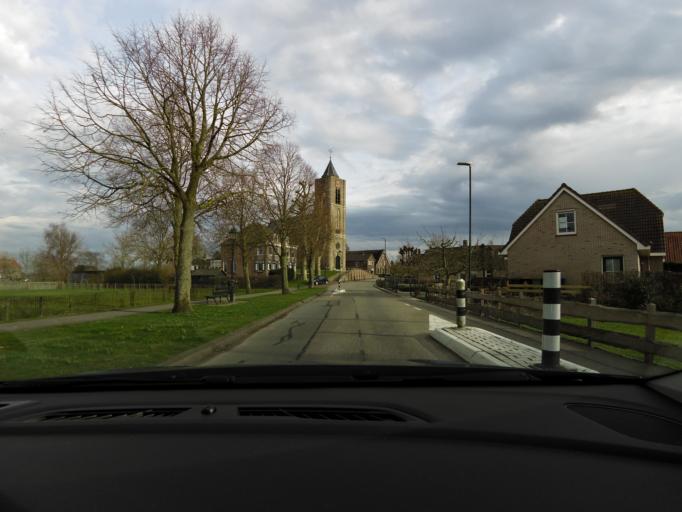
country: NL
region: South Holland
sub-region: Gemeente Gorinchem
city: Gorinchem
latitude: 51.8808
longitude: 4.9454
